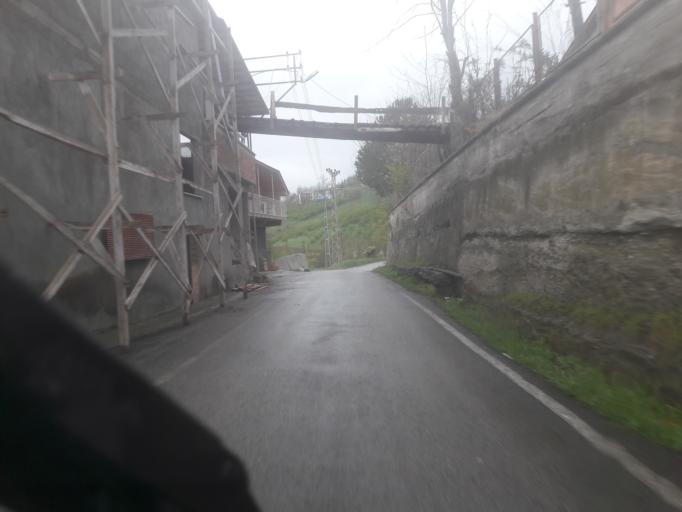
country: TR
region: Trabzon
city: Duzkoy
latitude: 40.9303
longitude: 39.4792
